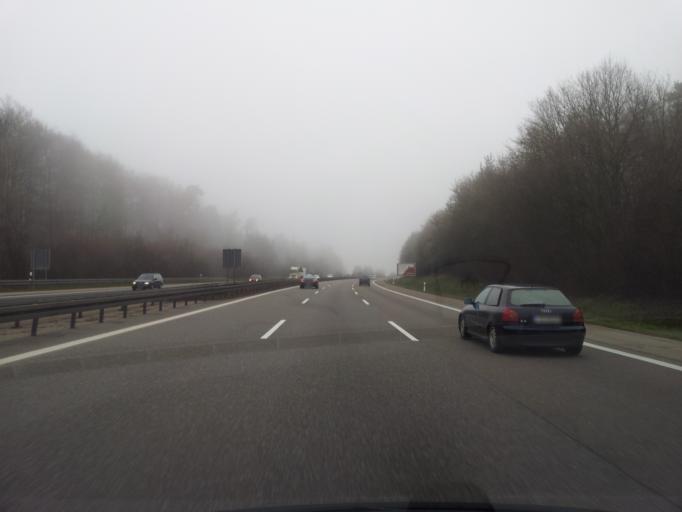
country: DE
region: Baden-Wuerttemberg
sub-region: Freiburg Region
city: Engen
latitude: 47.8727
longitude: 8.7770
